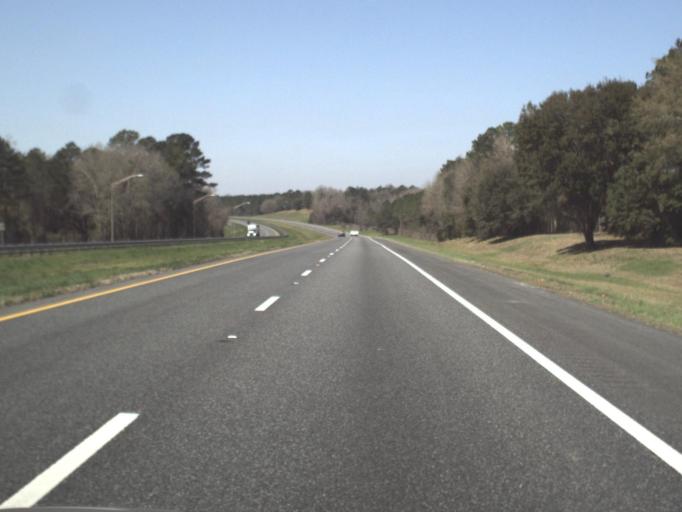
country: US
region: Florida
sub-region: Jackson County
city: Marianna
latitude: 30.7572
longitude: -85.3302
